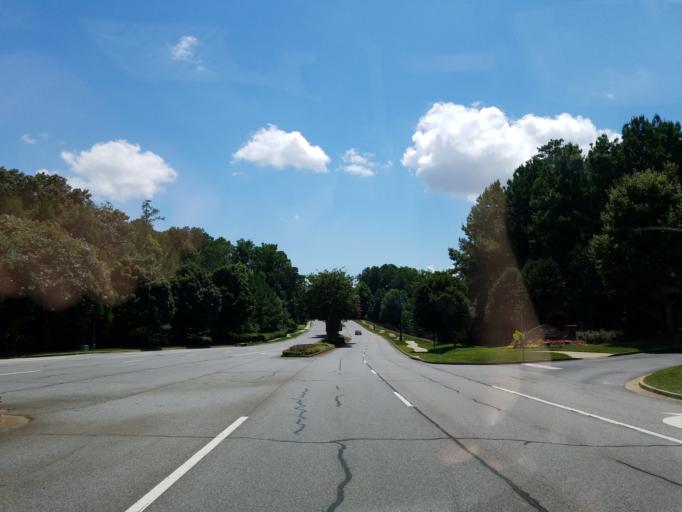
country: US
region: Georgia
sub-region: Fulton County
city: Alpharetta
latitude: 34.0947
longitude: -84.2618
